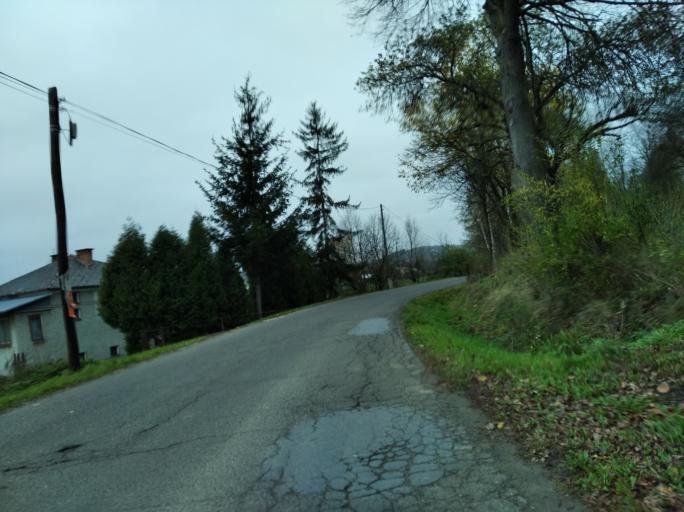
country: PL
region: Subcarpathian Voivodeship
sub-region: Powiat strzyzowski
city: Frysztak
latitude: 49.8351
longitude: 21.6252
